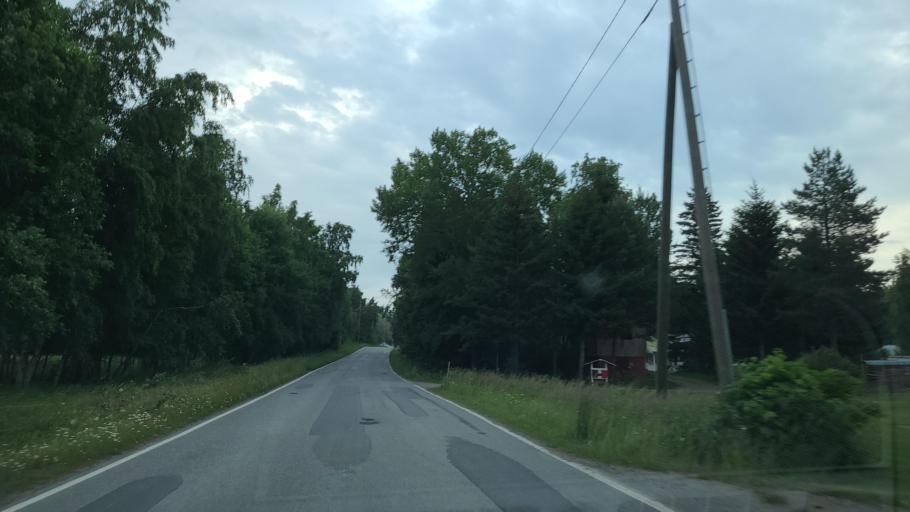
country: FI
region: Ostrobothnia
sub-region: Vaasa
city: Replot
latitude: 63.1884
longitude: 21.3005
